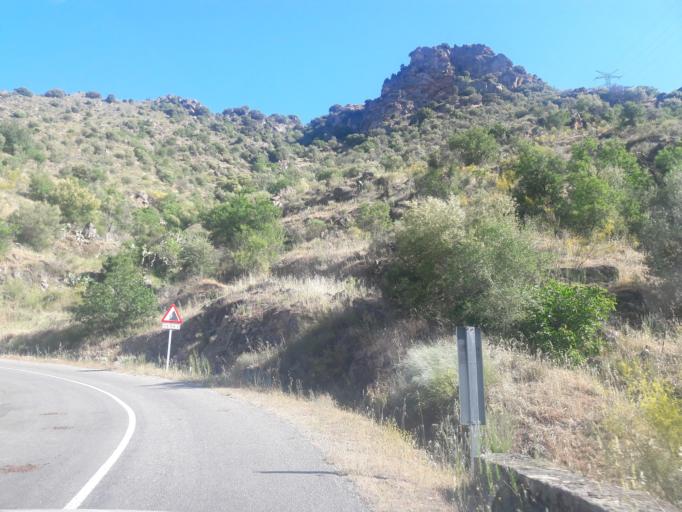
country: ES
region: Castille and Leon
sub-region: Provincia de Salamanca
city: Saucelle
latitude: 41.0303
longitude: -6.7305
